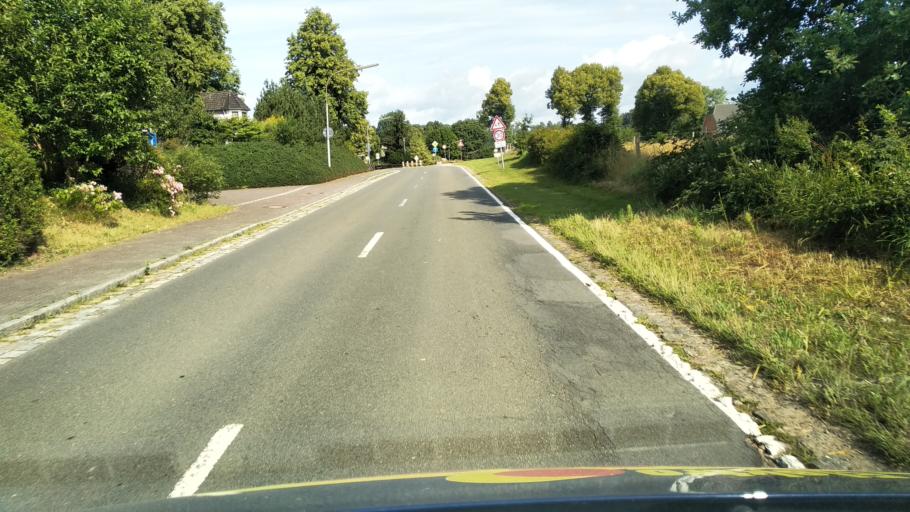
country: DE
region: Schleswig-Holstein
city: Brekendorf
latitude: 54.4195
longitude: 9.6313
